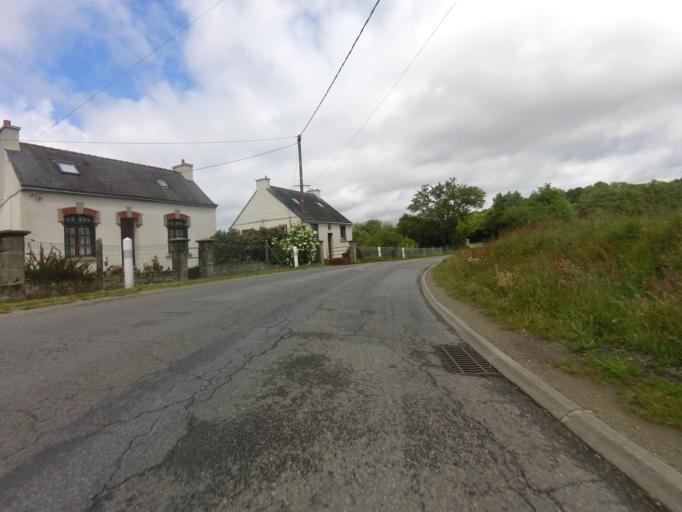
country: FR
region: Brittany
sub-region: Departement du Morbihan
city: Baden
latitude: 47.6042
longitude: -2.9159
